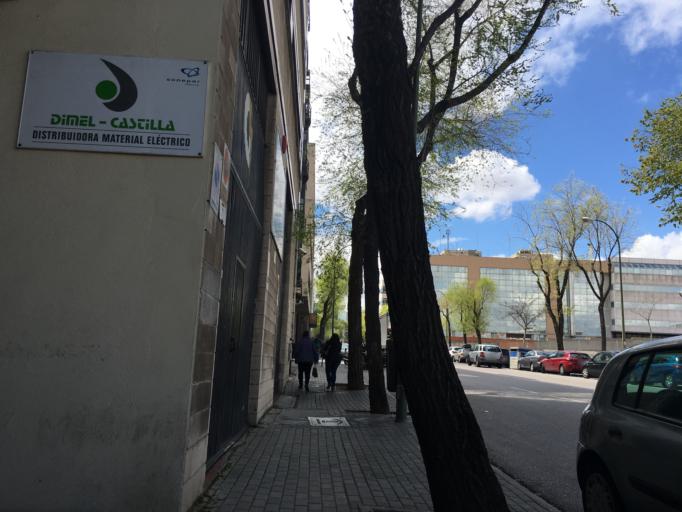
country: ES
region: Madrid
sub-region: Provincia de Madrid
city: San Blas
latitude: 40.4351
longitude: -3.6269
